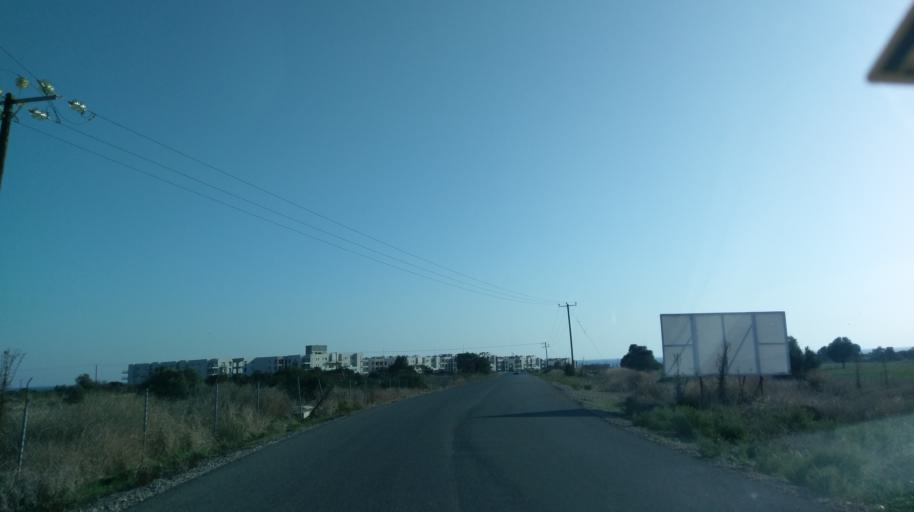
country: CY
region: Ammochostos
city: Leonarisso
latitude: 35.3340
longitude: 34.0616
